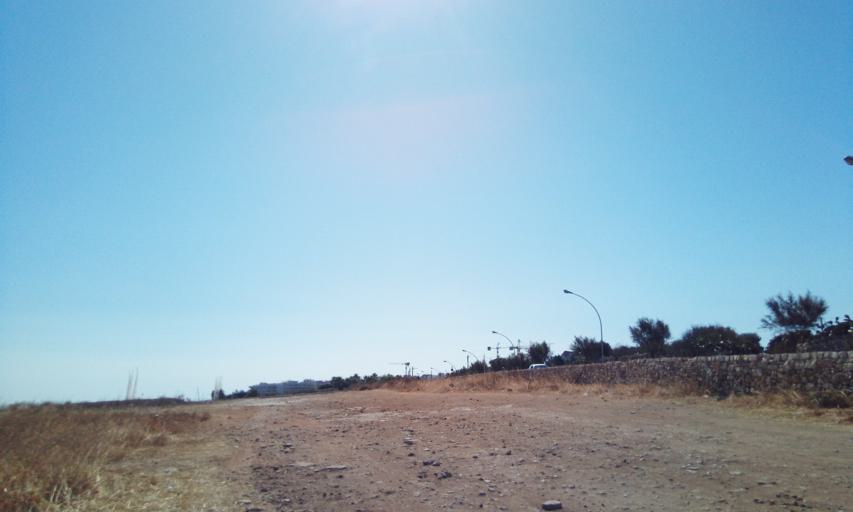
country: IT
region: Apulia
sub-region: Provincia di Bari
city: Polignano a Mare
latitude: 41.0001
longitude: 17.2081
